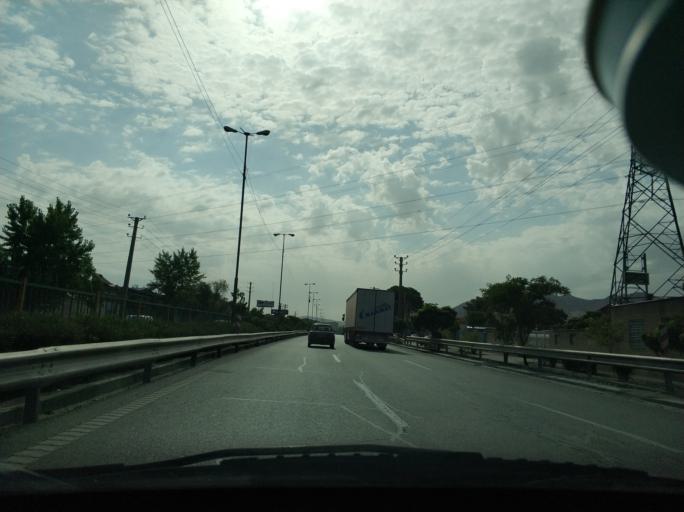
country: IR
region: Tehran
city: Tehran
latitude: 35.7262
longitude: 51.5583
